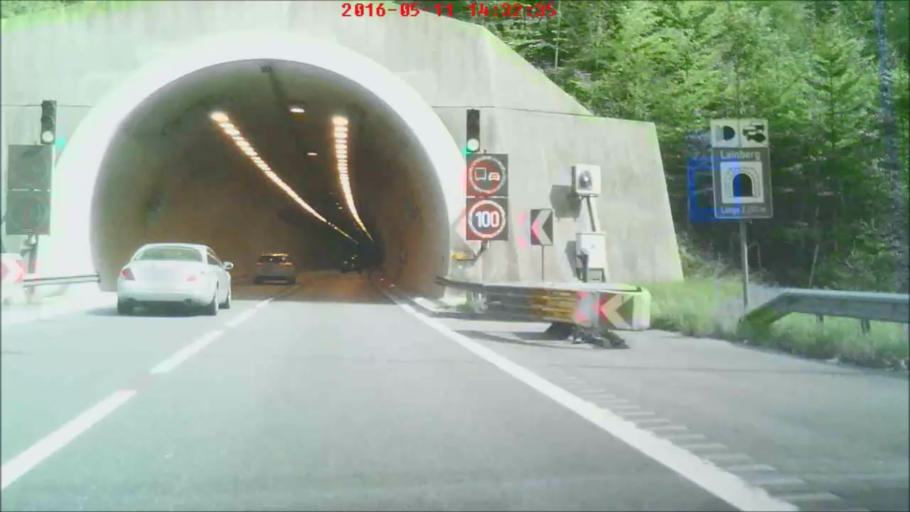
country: AT
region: Upper Austria
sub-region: Politischer Bezirk Kirchdorf an der Krems
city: Rossleithen
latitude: 47.7582
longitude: 14.2148
